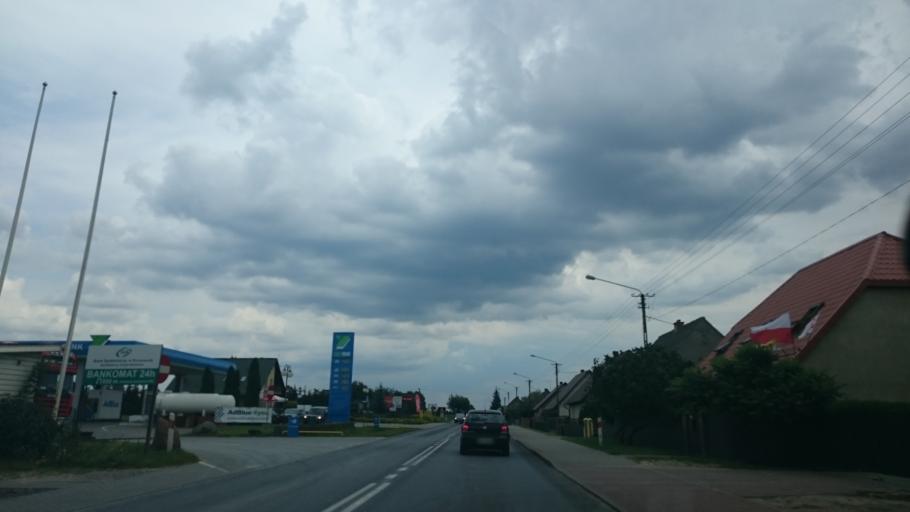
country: PL
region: Kujawsko-Pomorskie
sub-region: Powiat tucholski
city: Lubiewo
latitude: 53.5048
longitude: 18.0069
